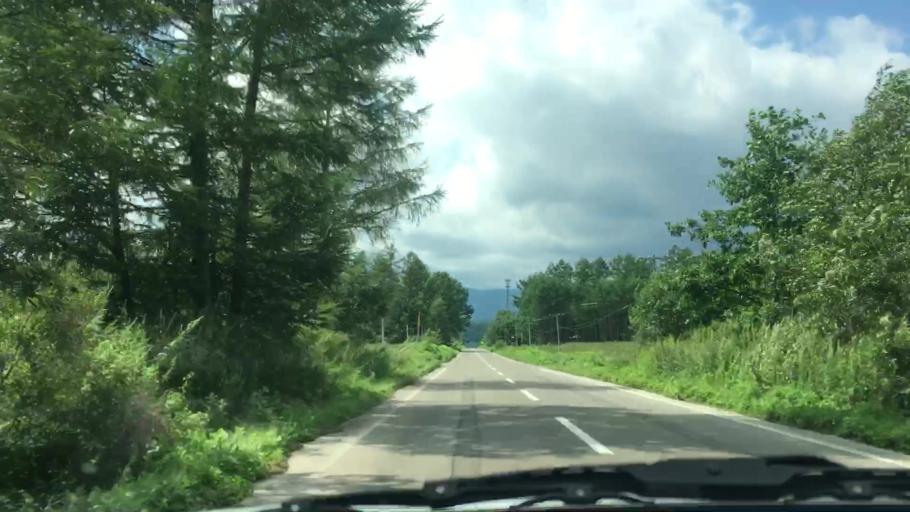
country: JP
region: Hokkaido
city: Otofuke
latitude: 43.2828
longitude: 143.3186
